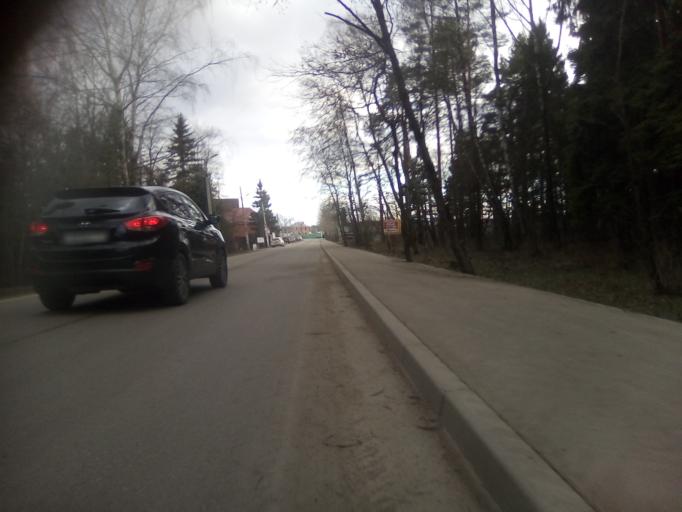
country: RU
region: Moskovskaya
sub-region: Leninskiy Rayon
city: Vnukovo
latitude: 55.5969
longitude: 37.3196
